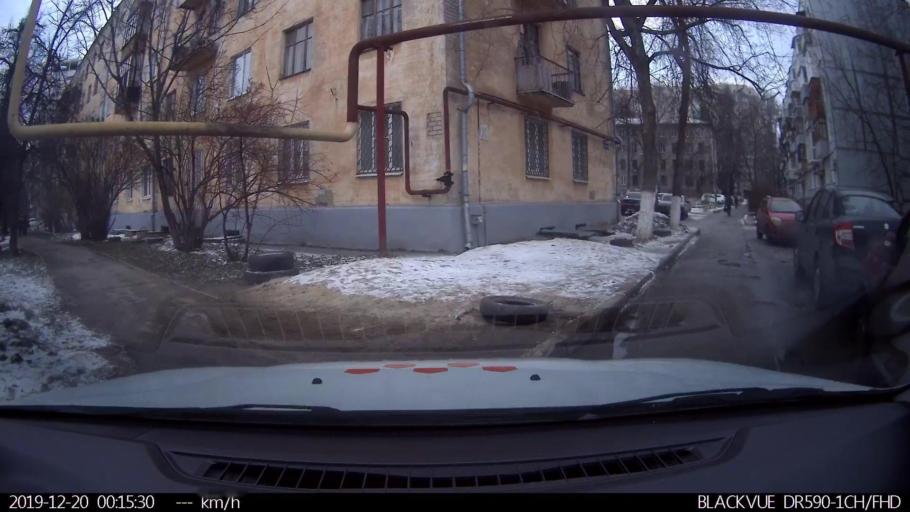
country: RU
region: Jaroslavl
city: Porech'ye-Rybnoye
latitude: 56.9871
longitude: 39.3905
